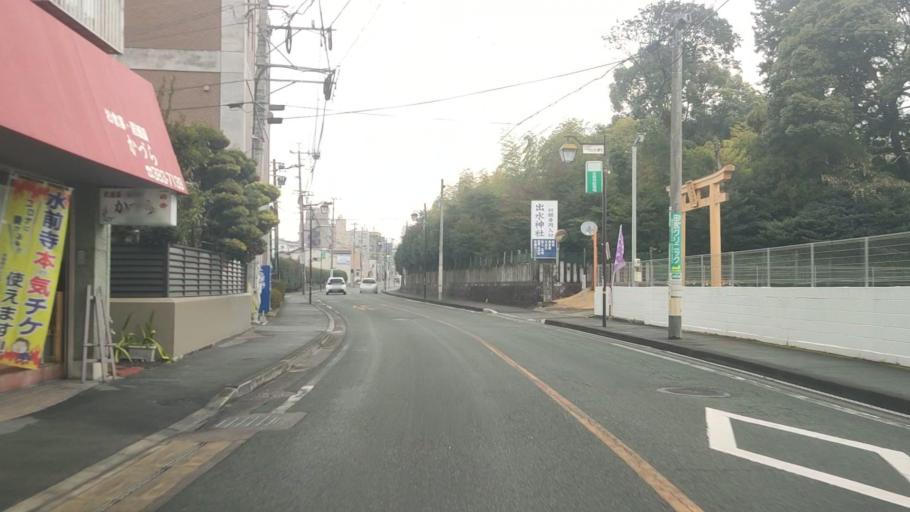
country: JP
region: Kumamoto
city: Kumamoto
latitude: 32.7923
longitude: 130.7336
